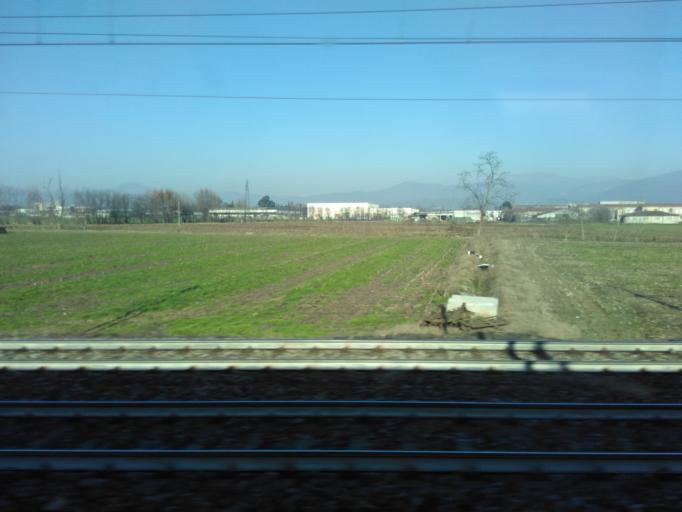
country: IT
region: Lombardy
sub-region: Provincia di Brescia
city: Ospitaletto
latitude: 45.5472
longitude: 10.0966
